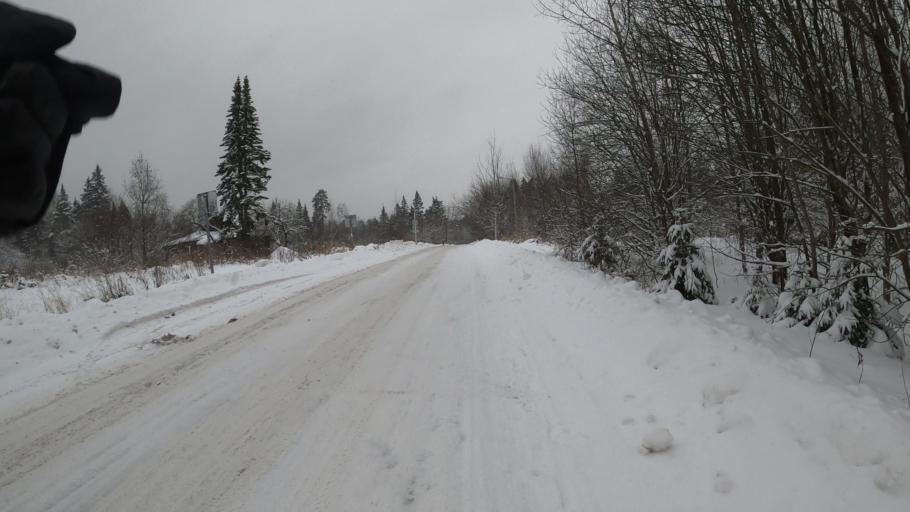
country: RU
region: Moskovskaya
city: Firsanovka
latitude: 55.9190
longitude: 37.2093
